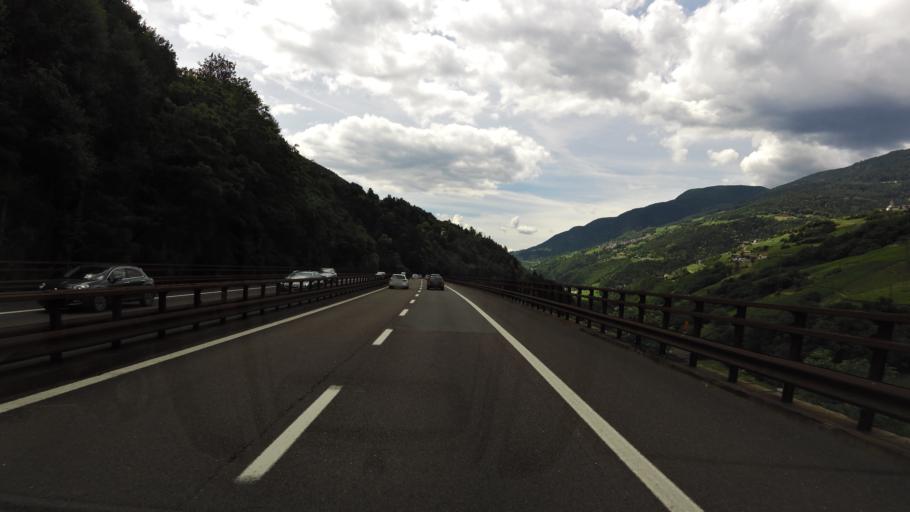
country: IT
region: Trentino-Alto Adige
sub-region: Bolzano
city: Villandro
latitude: 46.6281
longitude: 11.5511
